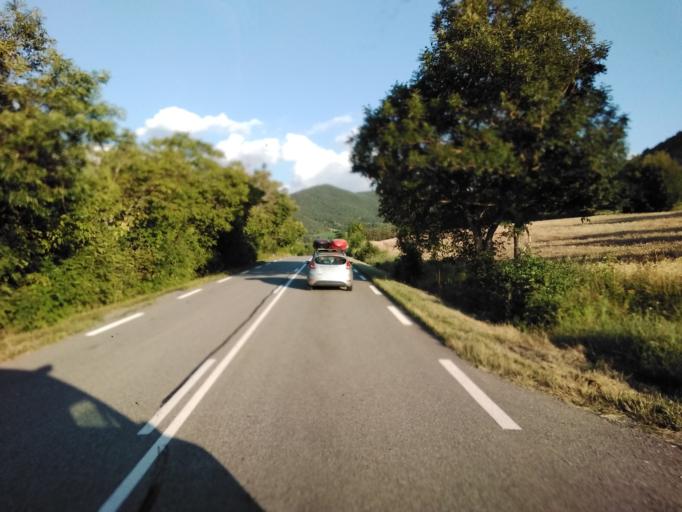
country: FR
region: Provence-Alpes-Cote d'Azur
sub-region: Departement des Hautes-Alpes
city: Chorges
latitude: 44.4552
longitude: 6.2938
